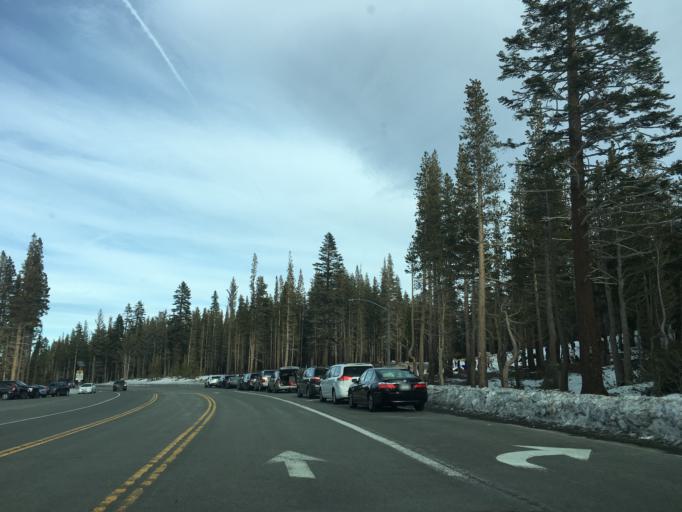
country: US
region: Nevada
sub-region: Washoe County
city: Incline Village
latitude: 39.3230
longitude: -119.8937
